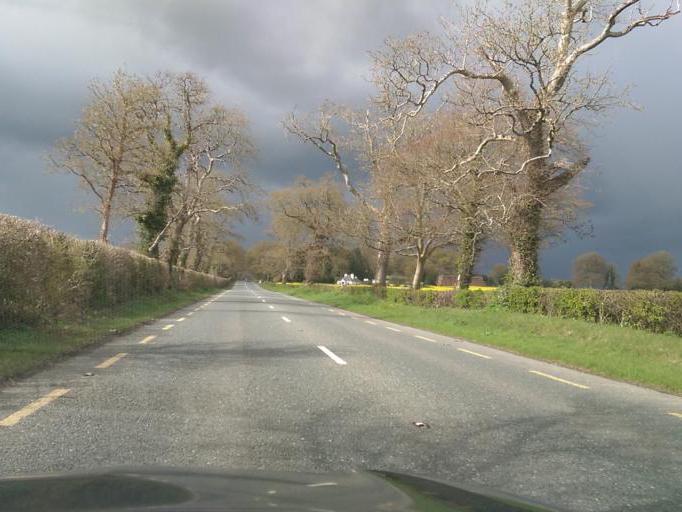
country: IE
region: Leinster
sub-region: An Mhi
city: Dunshaughlin
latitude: 53.5411
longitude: -6.5668
